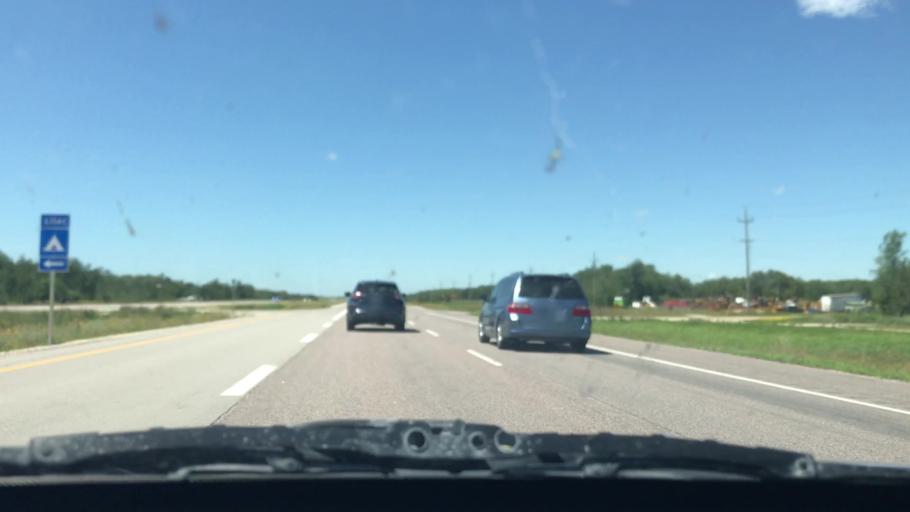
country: CA
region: Manitoba
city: Steinbach
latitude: 49.6800
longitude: -96.5937
